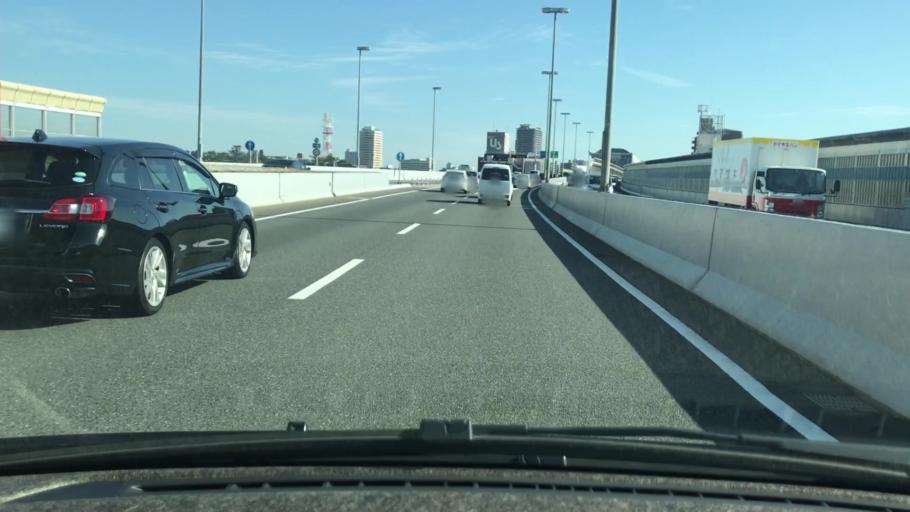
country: JP
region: Hyogo
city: Nishinomiya-hama
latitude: 34.7332
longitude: 135.3253
